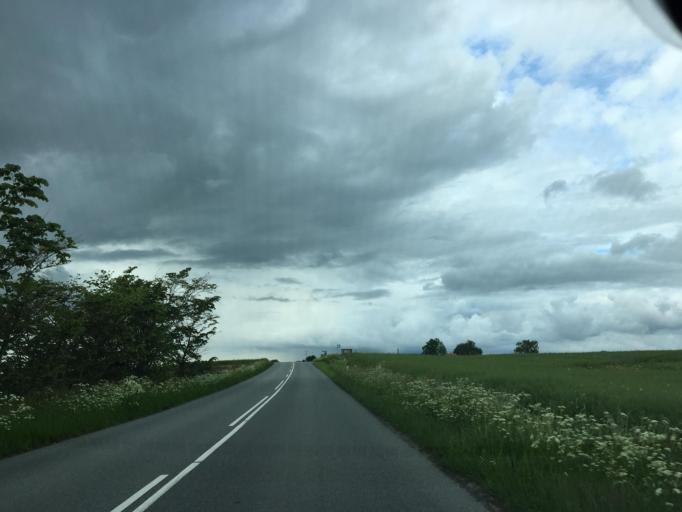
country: DK
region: Capital Region
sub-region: Frederikssund Kommune
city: Slangerup
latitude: 55.8621
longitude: 12.1784
